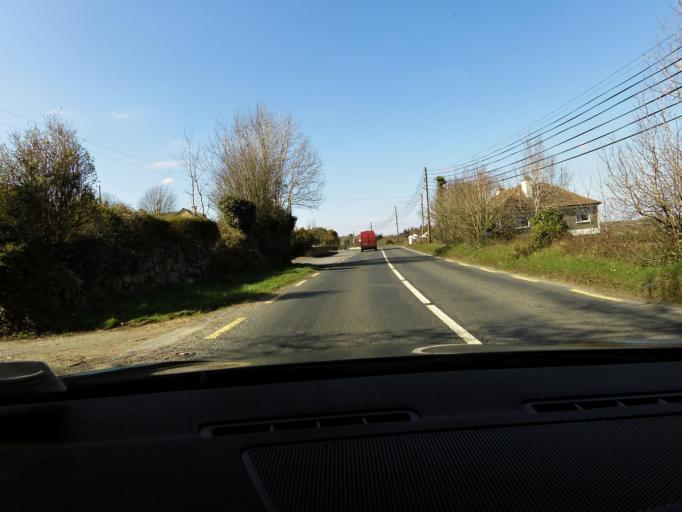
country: IE
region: Connaught
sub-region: County Galway
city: Moycullen
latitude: 53.3234
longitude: -9.1640
